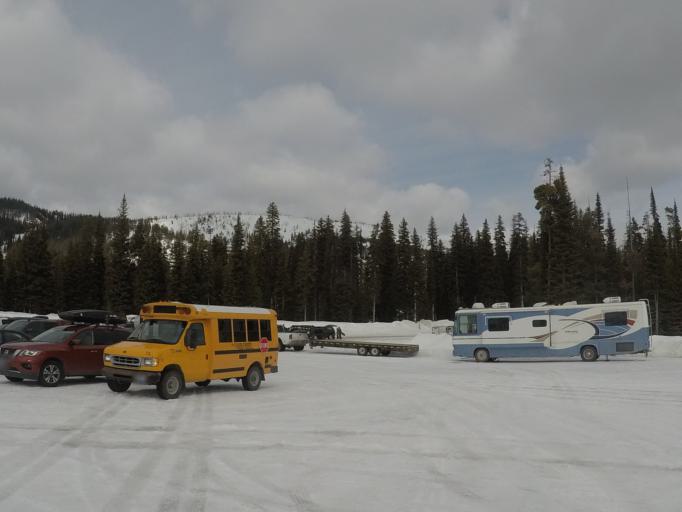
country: US
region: Idaho
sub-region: Lemhi County
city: Salmon
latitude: 45.6932
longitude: -113.9513
